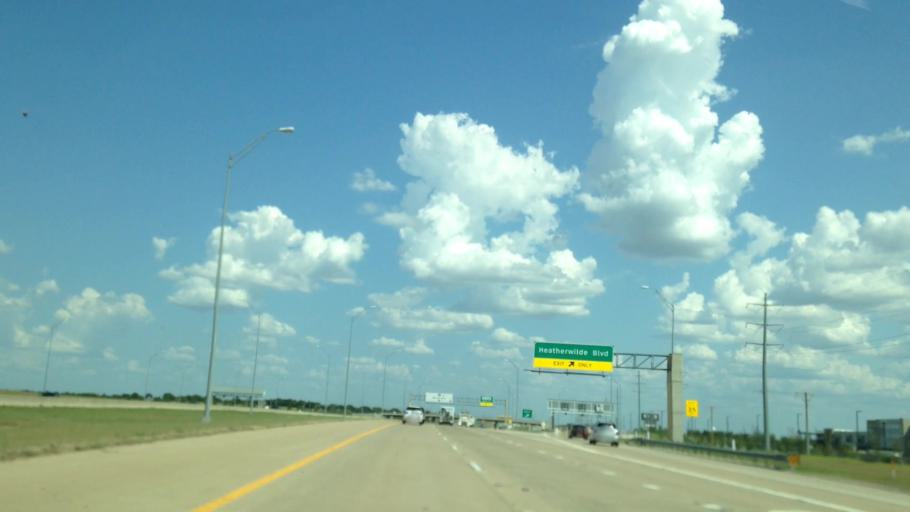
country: US
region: Texas
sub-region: Travis County
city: Windemere
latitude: 30.4873
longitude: -97.6202
